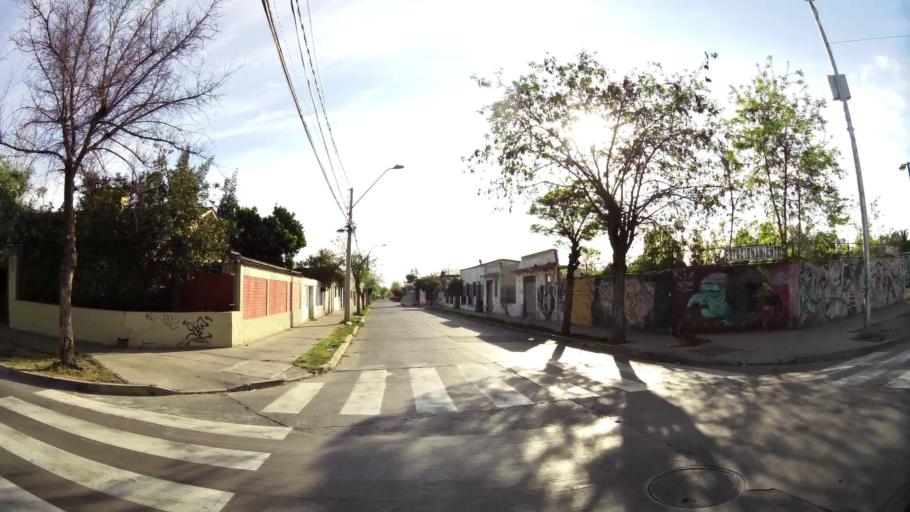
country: CL
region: Santiago Metropolitan
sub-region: Provincia de Cordillera
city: Puente Alto
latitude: -33.6110
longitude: -70.5789
